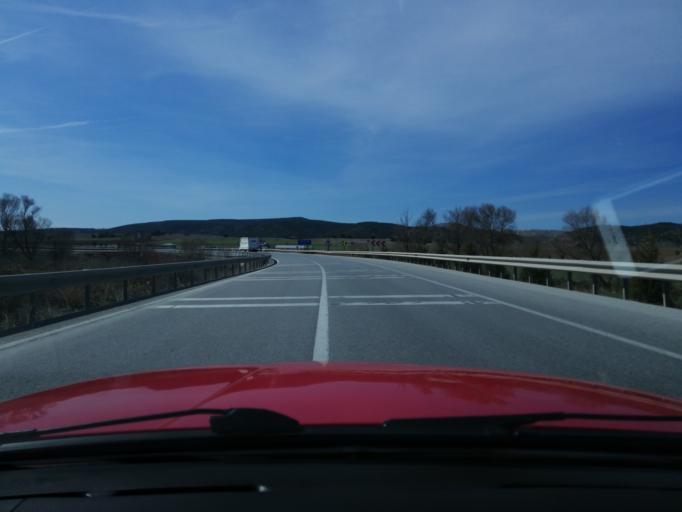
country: TR
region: Kuetahya
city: Sabuncu
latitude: 39.6826
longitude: 30.1534
